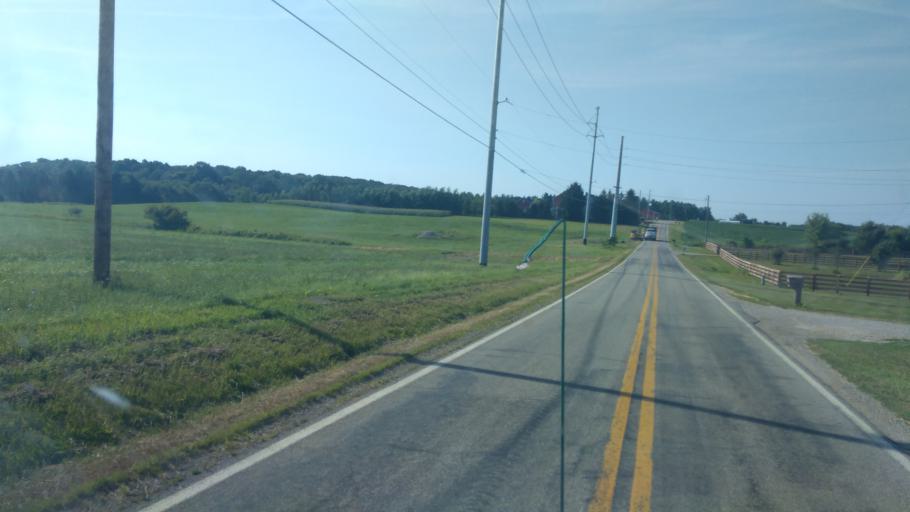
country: US
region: Ohio
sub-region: Delaware County
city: Delaware
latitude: 40.3462
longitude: -83.0540
